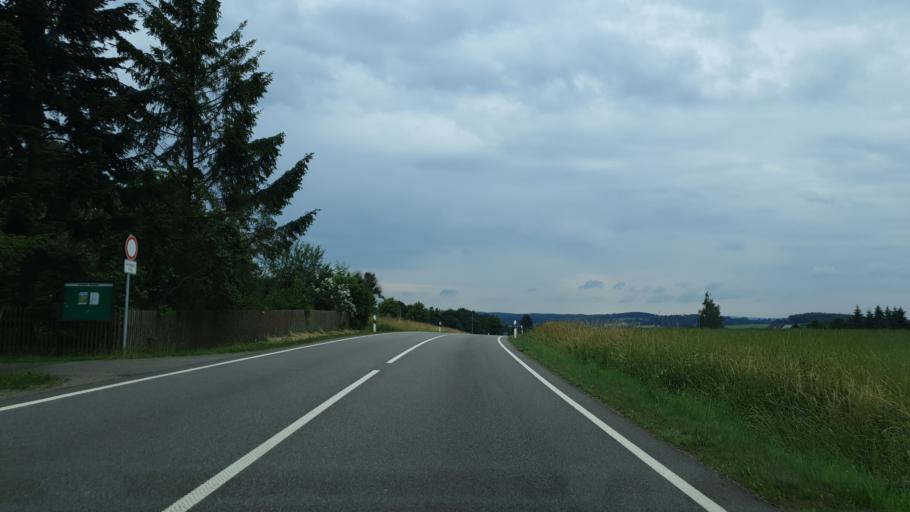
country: DE
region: Saxony
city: Hirschfeld
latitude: 50.6255
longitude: 12.4324
